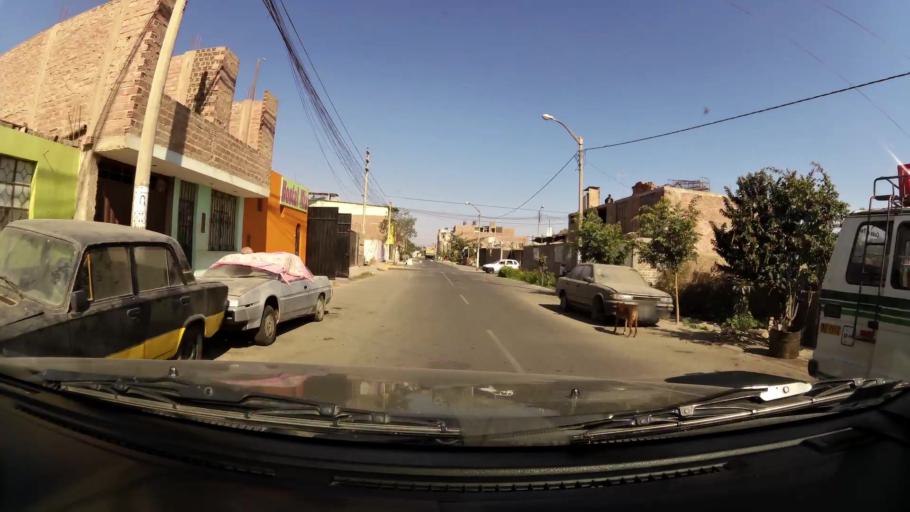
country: PE
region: Ica
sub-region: Provincia de Ica
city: La Tinguina
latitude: -14.0423
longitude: -75.7102
